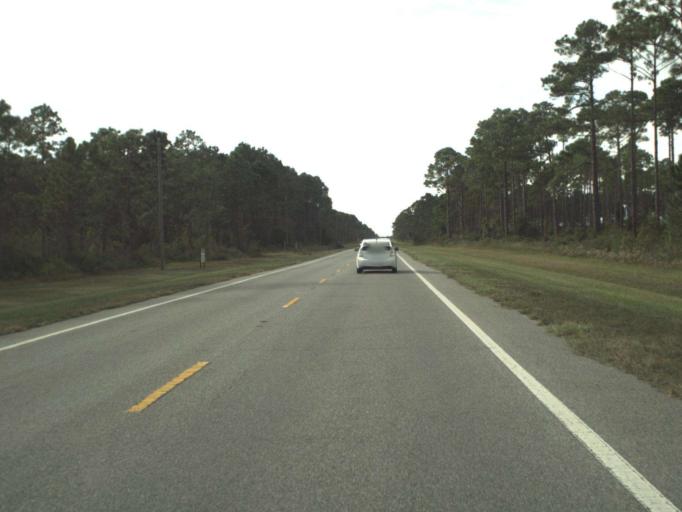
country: US
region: Florida
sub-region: Bay County
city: Tyndall Air Force Base
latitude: 30.0454
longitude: -85.5584
